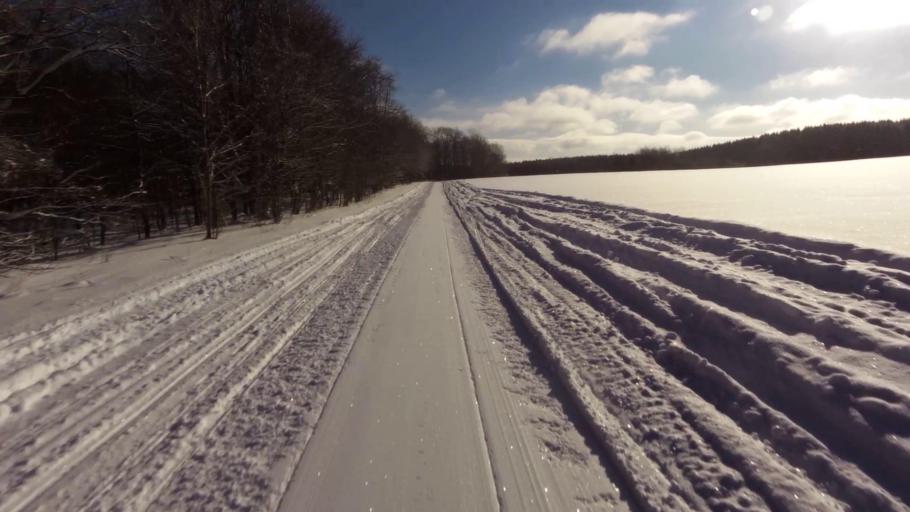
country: US
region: New York
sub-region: Chautauqua County
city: Falconer
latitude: 42.2682
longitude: -79.1884
